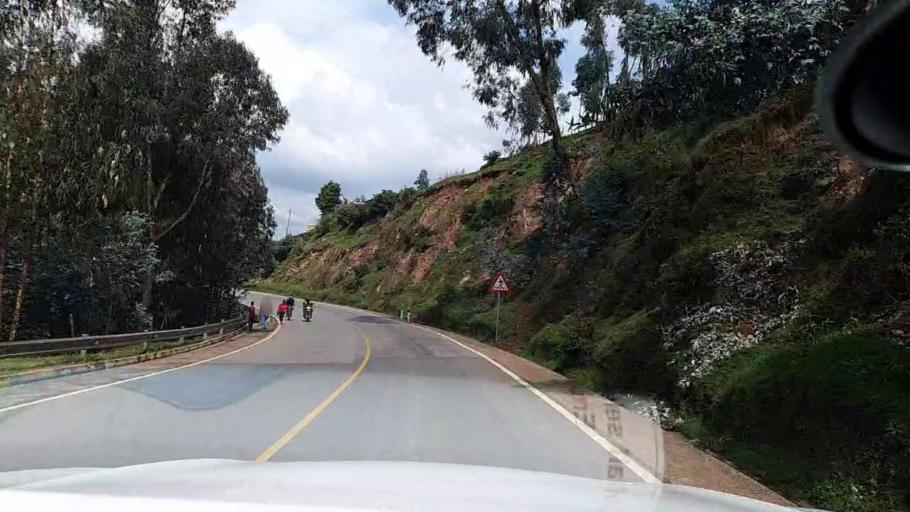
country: RW
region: Southern Province
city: Nzega
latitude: -2.4836
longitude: 29.5216
